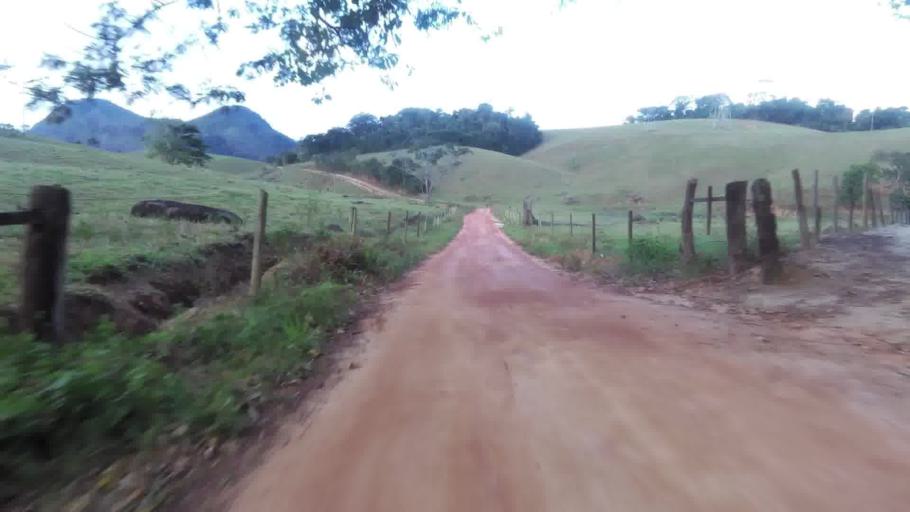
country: BR
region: Espirito Santo
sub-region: Guarapari
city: Guarapari
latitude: -20.6711
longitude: -40.6128
